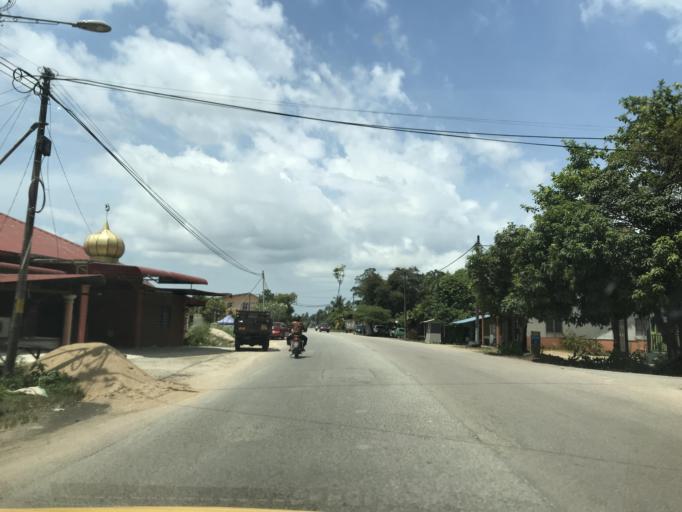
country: MY
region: Kelantan
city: Pasir Mas
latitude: 6.0503
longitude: 102.1822
